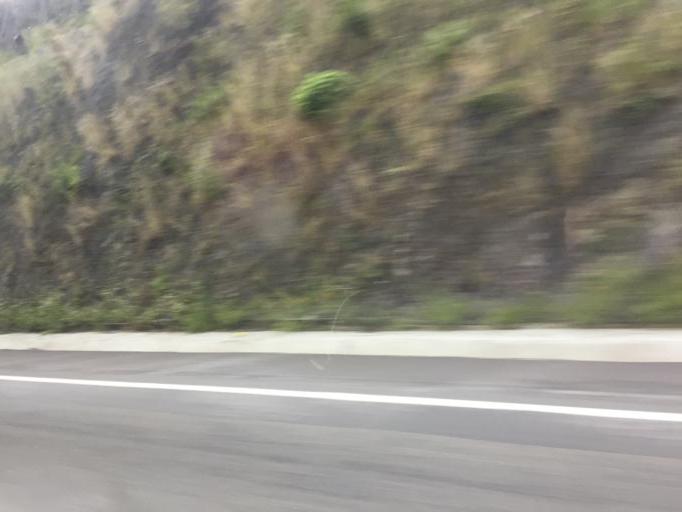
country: MX
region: Jalisco
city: Ocotlan
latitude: 20.4319
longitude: -102.7873
